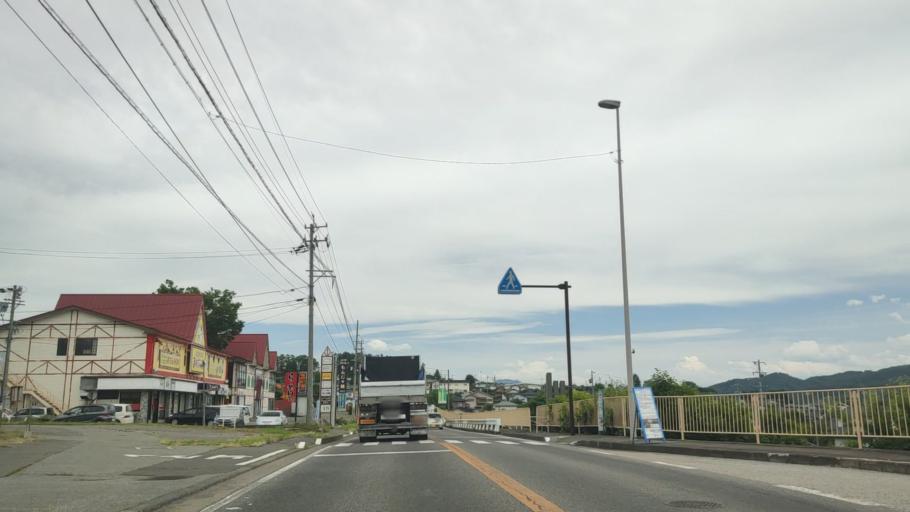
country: JP
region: Nagano
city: Komoro
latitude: 36.3446
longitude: 138.3805
